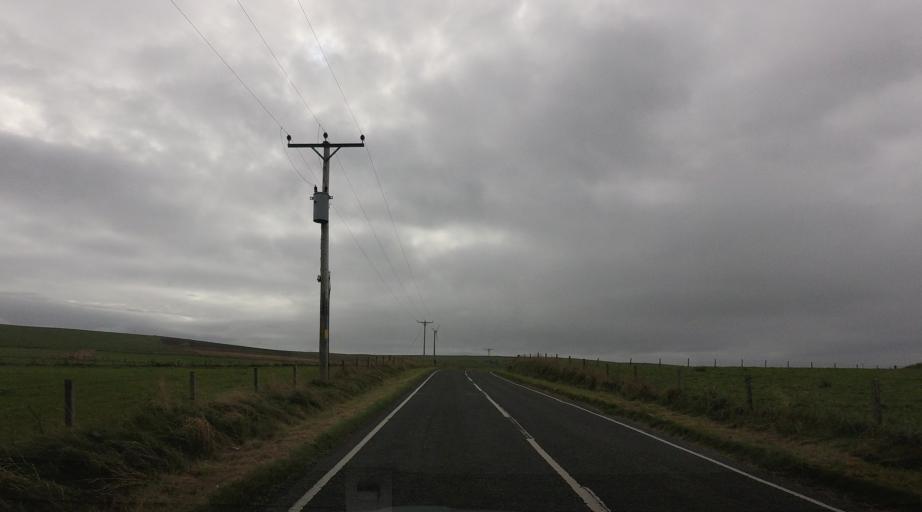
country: GB
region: Scotland
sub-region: Orkney Islands
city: Orkney
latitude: 58.7859
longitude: -2.9586
